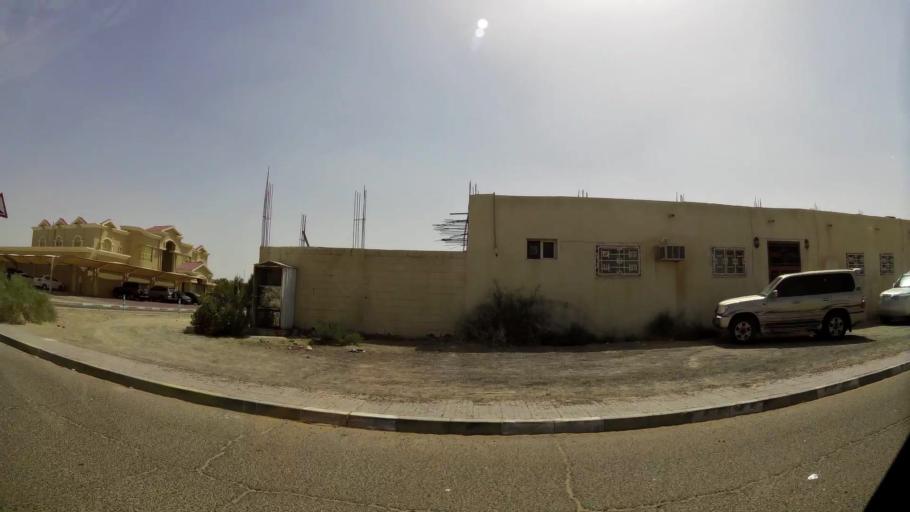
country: AE
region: Abu Dhabi
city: Al Ain
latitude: 24.2265
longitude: 55.6925
